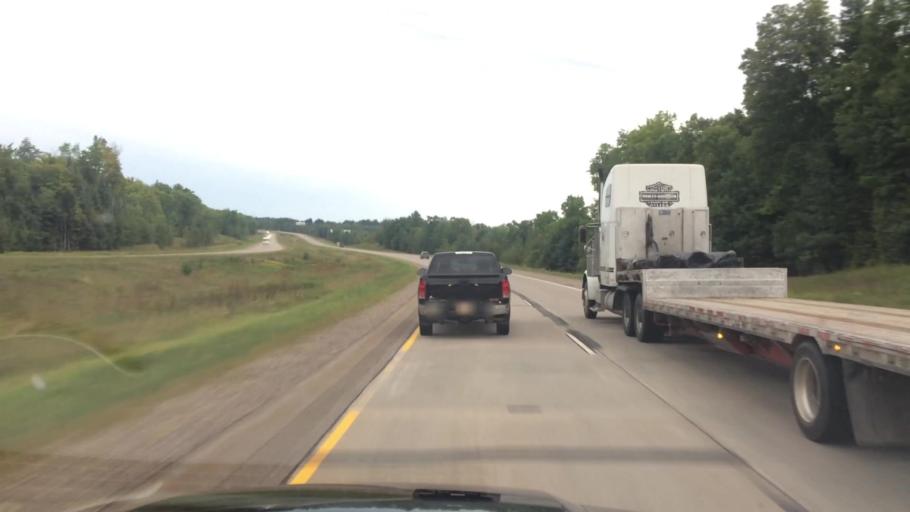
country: US
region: Wisconsin
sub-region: Lincoln County
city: Merrill
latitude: 45.3285
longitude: -89.6790
